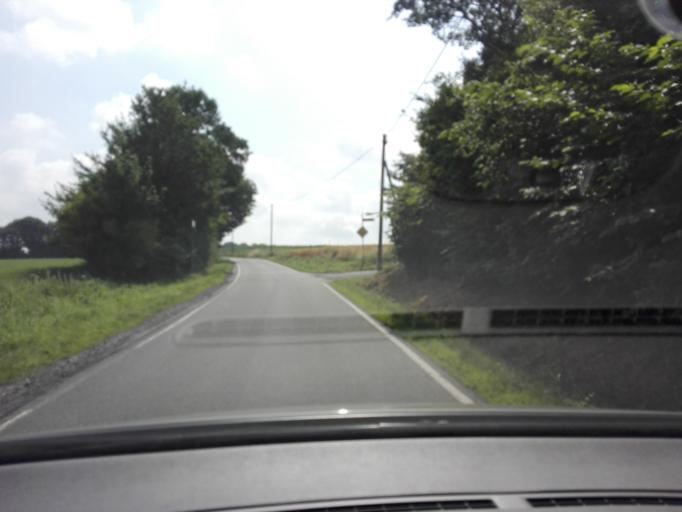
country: DE
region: North Rhine-Westphalia
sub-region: Regierungsbezirk Arnsberg
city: Frondenberg
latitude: 51.5145
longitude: 7.7515
